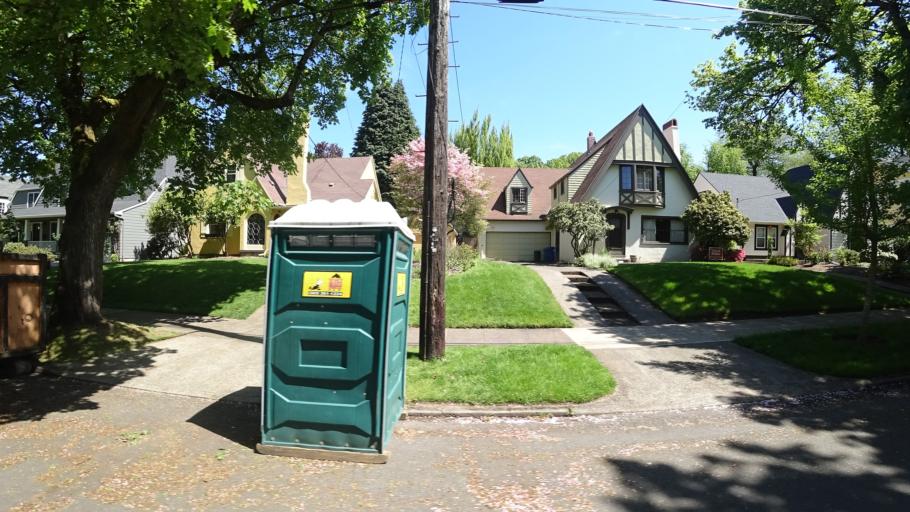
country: US
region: Oregon
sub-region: Clackamas County
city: Milwaukie
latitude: 45.4698
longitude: -122.6304
